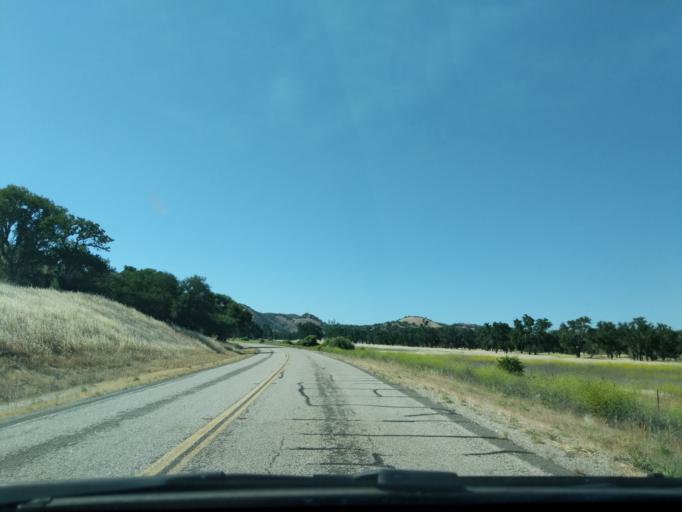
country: US
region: California
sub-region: Monterey County
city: King City
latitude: 36.0328
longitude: -121.1778
